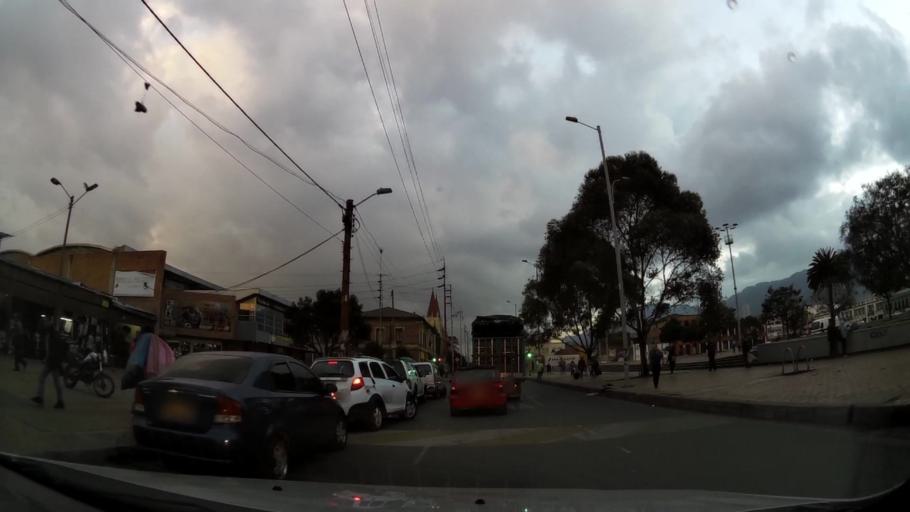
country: CO
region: Bogota D.C.
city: Bogota
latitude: 4.6048
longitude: -74.0864
